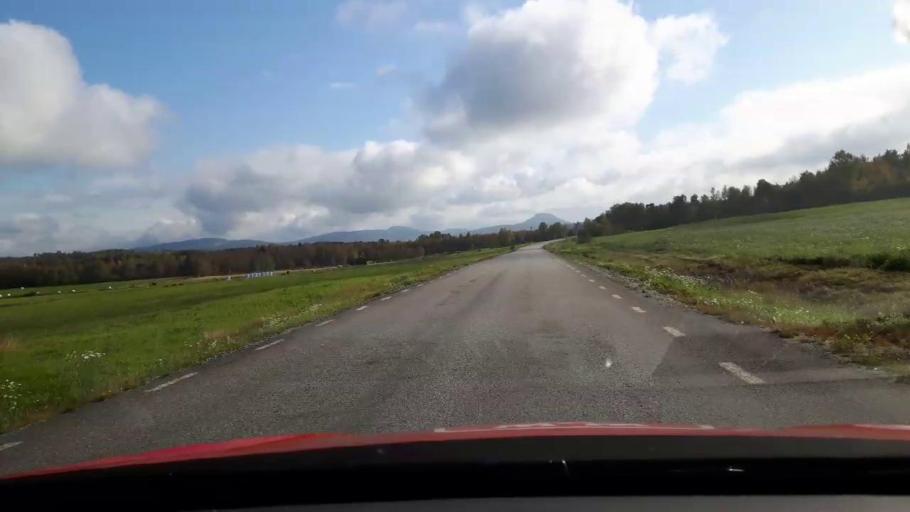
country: SE
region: Gaevleborg
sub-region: Ljusdals Kommun
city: Ljusdal
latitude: 61.7607
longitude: 16.0875
